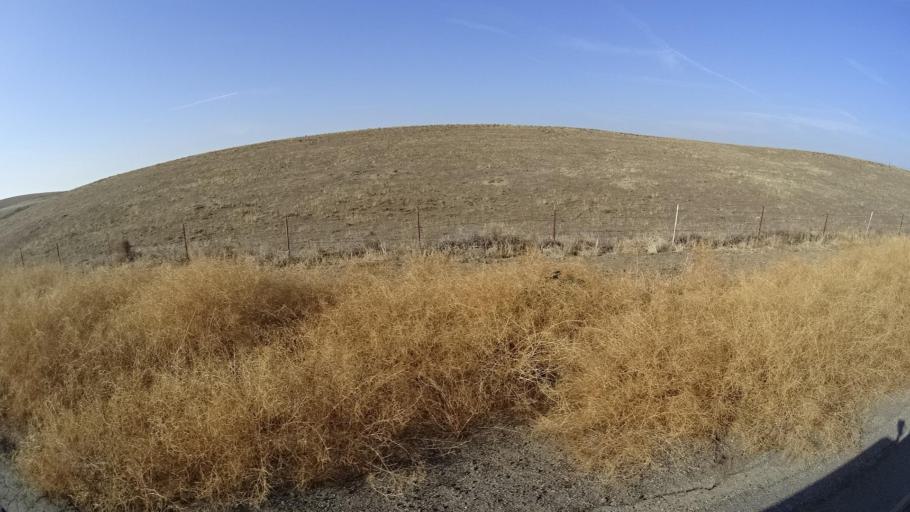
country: US
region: California
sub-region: Tulare County
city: Richgrove
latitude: 35.6236
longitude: -119.0299
